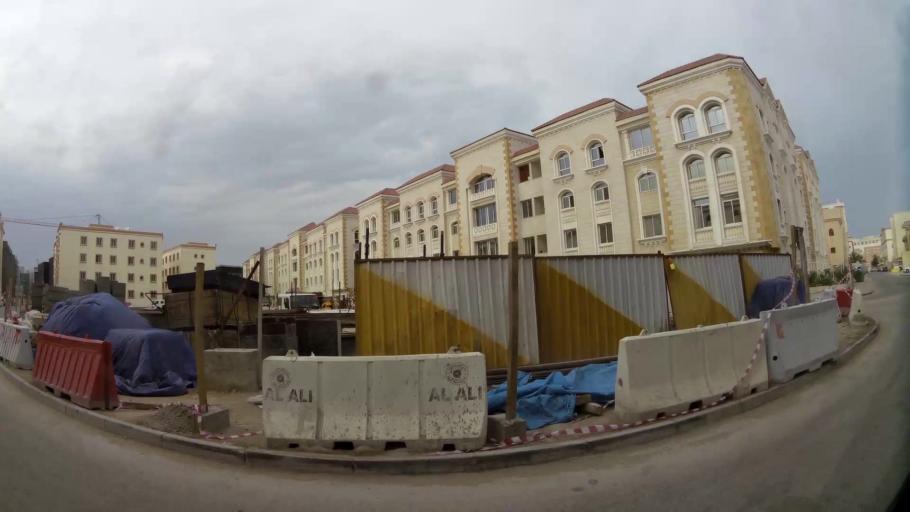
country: QA
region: Baladiyat ad Dawhah
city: Doha
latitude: 25.2751
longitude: 51.4938
